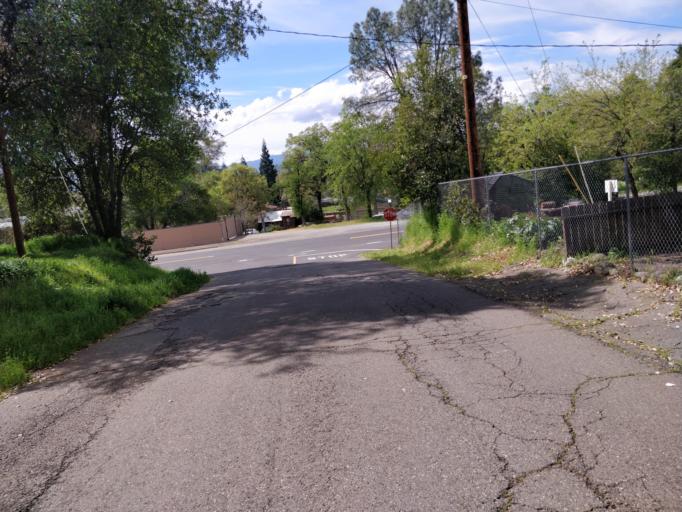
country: US
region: California
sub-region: Shasta County
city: Shasta Lake
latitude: 40.6757
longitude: -122.3533
